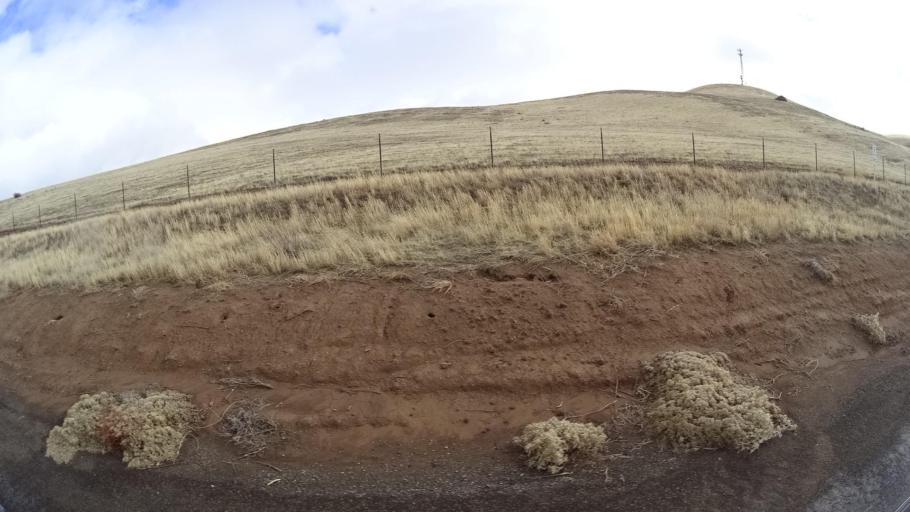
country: US
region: California
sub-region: Kern County
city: Maricopa
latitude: 34.9227
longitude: -119.4098
